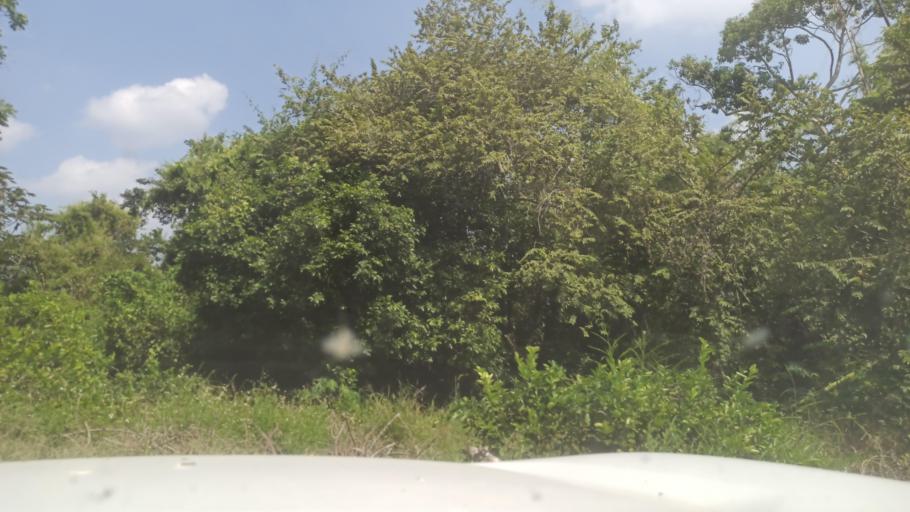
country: MX
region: Veracruz
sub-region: Atzalan
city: Colonias Pedernales
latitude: 20.0538
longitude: -96.9963
